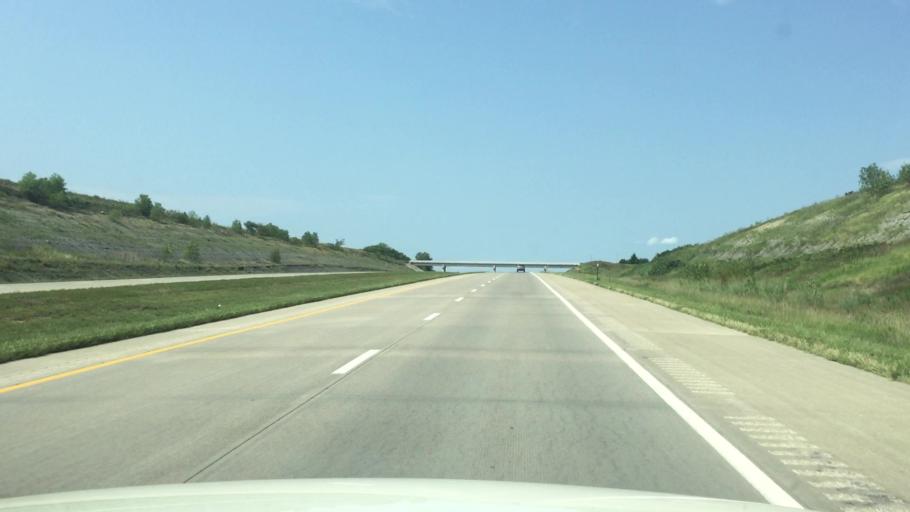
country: US
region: Kansas
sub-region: Linn County
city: Pleasanton
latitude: 38.1054
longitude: -94.7134
